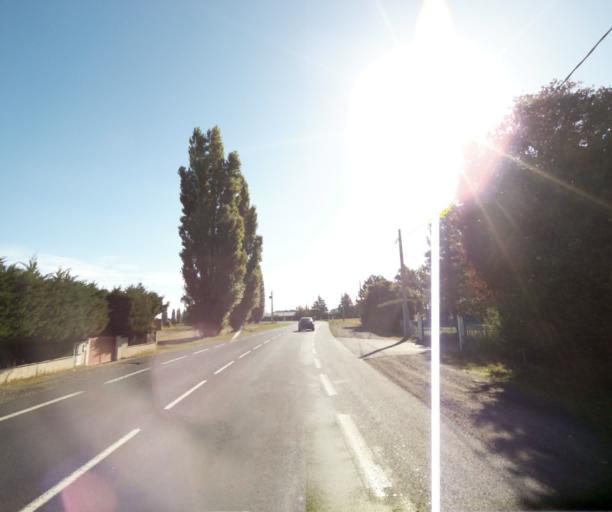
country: FR
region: Auvergne
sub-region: Departement du Puy-de-Dome
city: Gerzat
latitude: 45.8141
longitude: 3.1593
